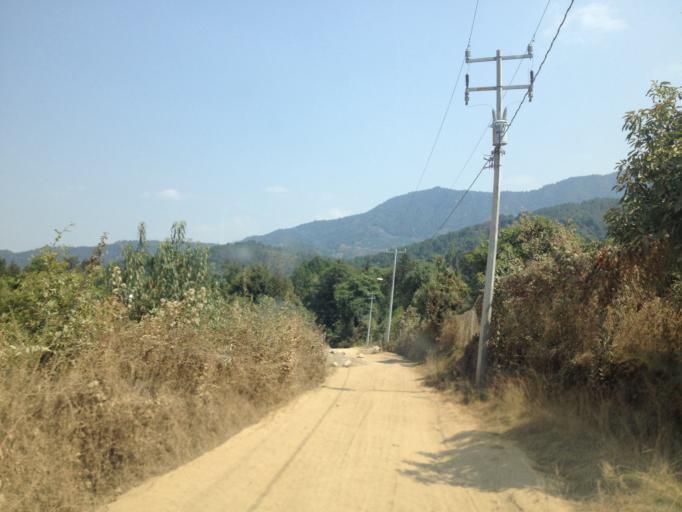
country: MX
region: Michoacan
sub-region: Zitacuaro
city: Macutzio
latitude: 19.4920
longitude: -100.3300
